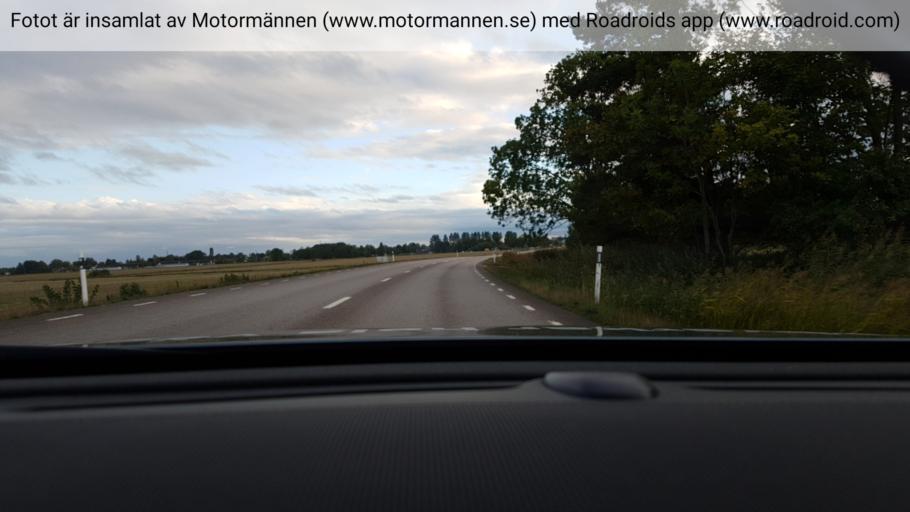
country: SE
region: Vaestra Goetaland
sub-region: Melleruds Kommun
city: Mellerud
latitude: 58.7130
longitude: 12.4561
